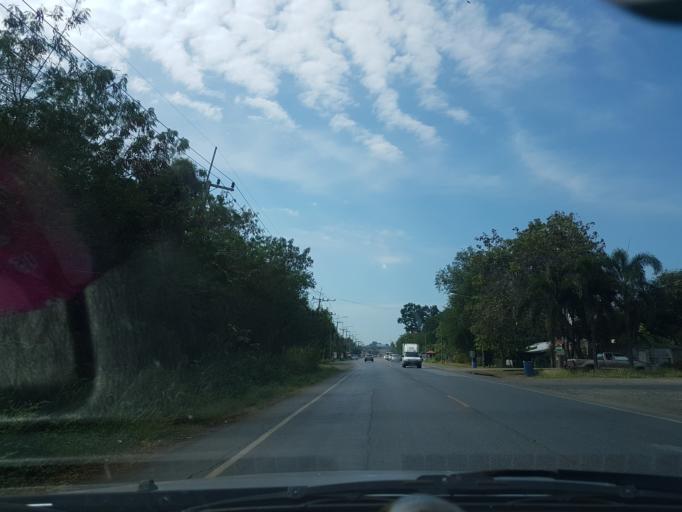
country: TH
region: Lop Buri
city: Lop Buri
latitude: 14.8003
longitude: 100.7304
